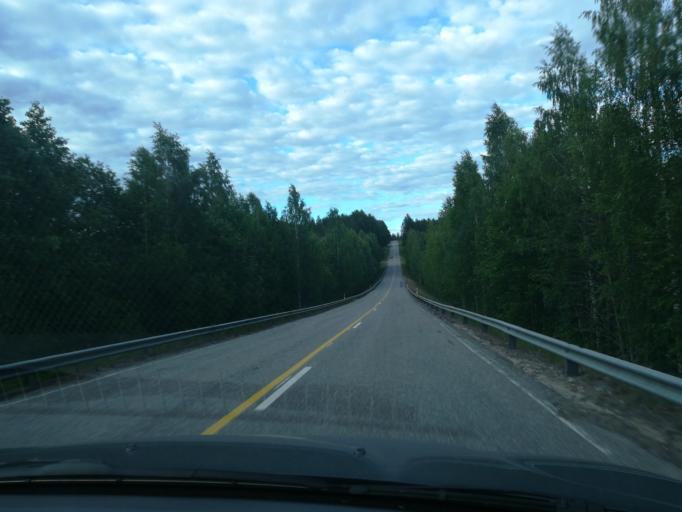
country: FI
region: Southern Savonia
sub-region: Mikkeli
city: Puumala
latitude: 61.5642
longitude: 28.1159
